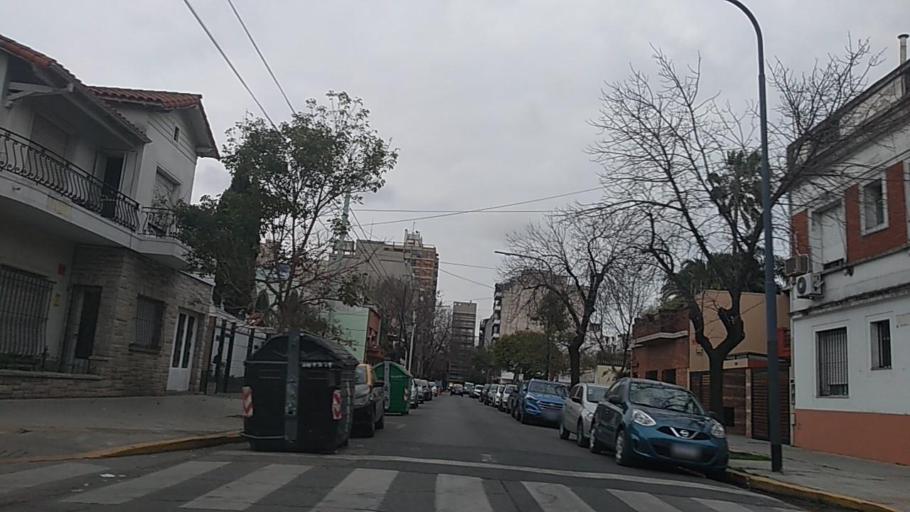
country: AR
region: Buenos Aires F.D.
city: Villa Santa Rita
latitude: -34.6082
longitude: -58.5113
